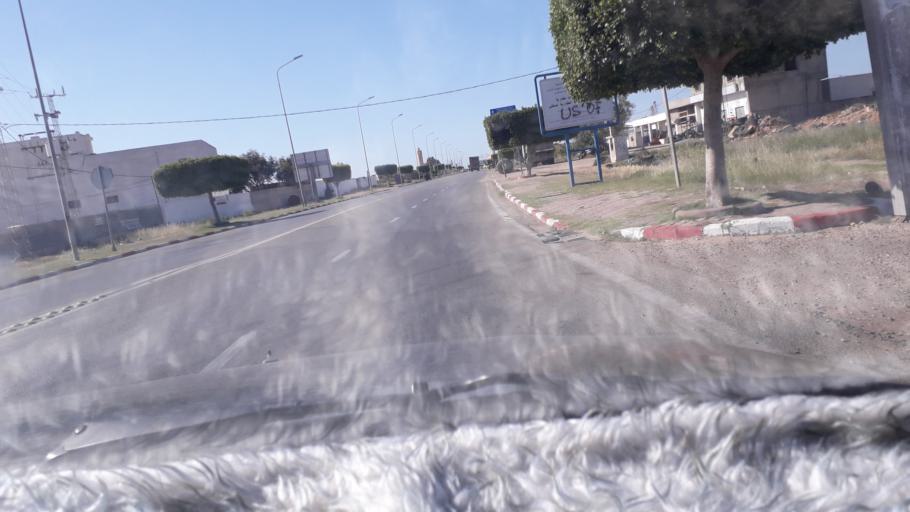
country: TN
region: Safaqis
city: Al Qarmadah
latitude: 34.8554
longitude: 10.7605
